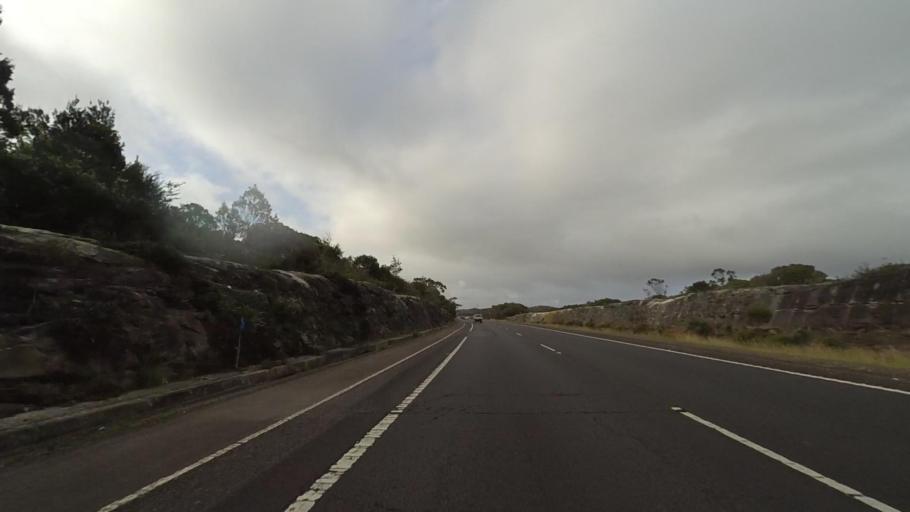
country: AU
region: New South Wales
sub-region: Wollongong
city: Bulli
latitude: -34.2792
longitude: 150.9281
